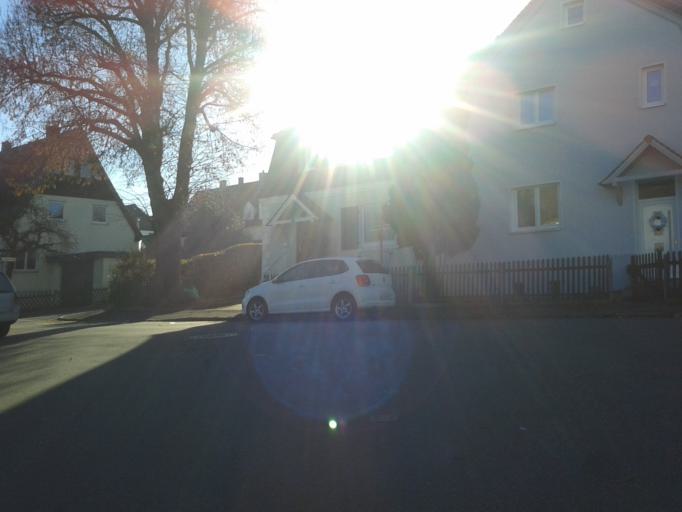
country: DE
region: Baden-Wuerttemberg
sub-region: Tuebingen Region
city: Ulm
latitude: 48.3900
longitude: 9.9671
